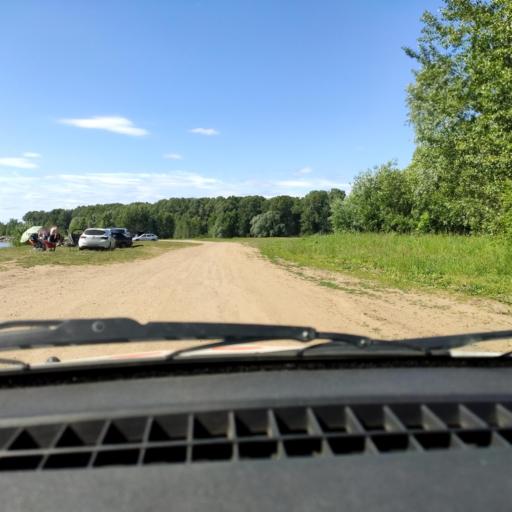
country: RU
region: Bashkortostan
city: Iglino
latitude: 54.7957
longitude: 56.2315
